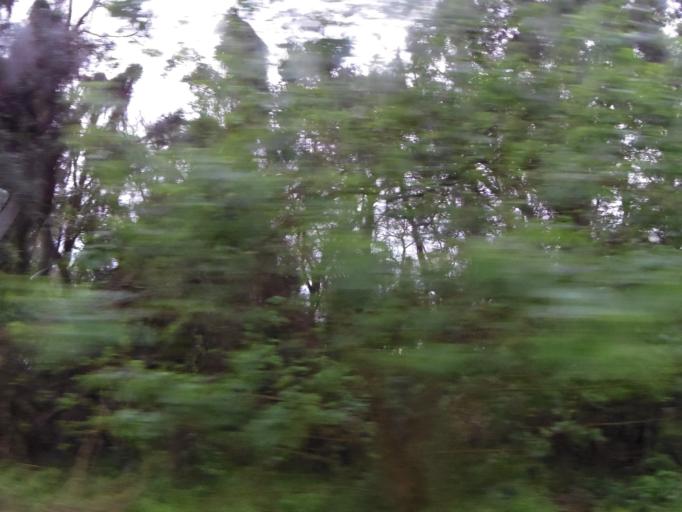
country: US
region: Florida
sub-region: Duval County
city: Jacksonville
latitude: 30.3291
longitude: -81.6985
